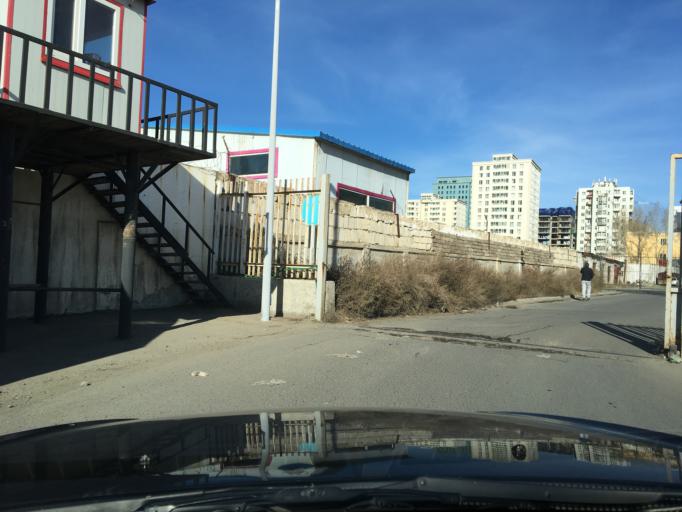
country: MN
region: Ulaanbaatar
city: Ulaanbaatar
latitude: 47.8953
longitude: 106.8975
